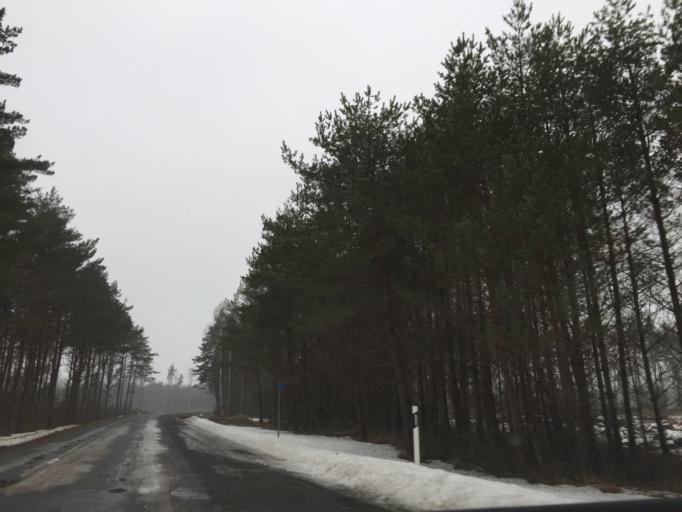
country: EE
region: Saare
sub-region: Kuressaare linn
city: Kuressaare
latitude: 58.3182
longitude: 22.7891
